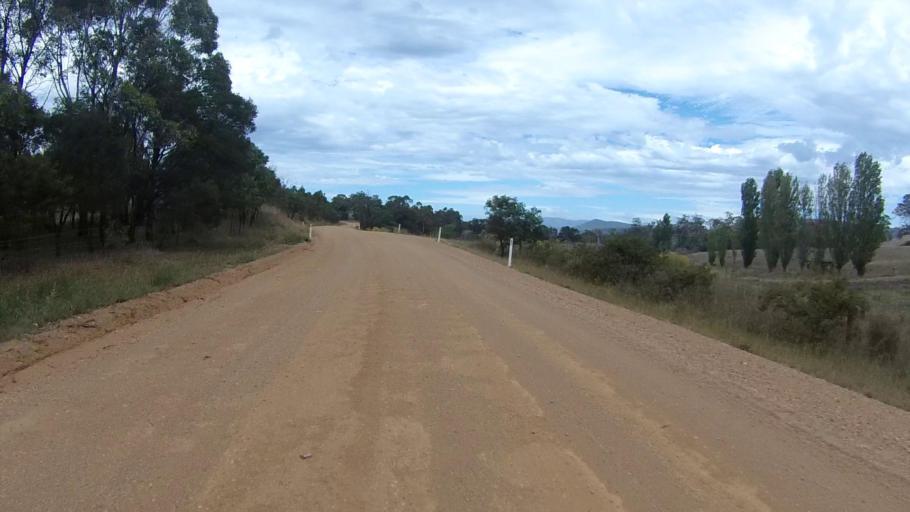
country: AU
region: Tasmania
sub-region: Sorell
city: Sorell
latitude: -42.6951
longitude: 147.4636
